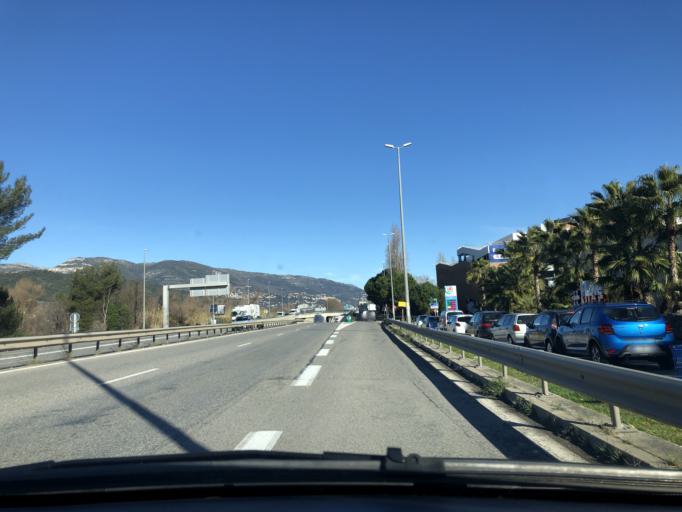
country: FR
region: Provence-Alpes-Cote d'Azur
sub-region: Departement des Alpes-Maritimes
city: Saint-Laurent-du-Var
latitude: 43.7084
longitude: 7.1881
